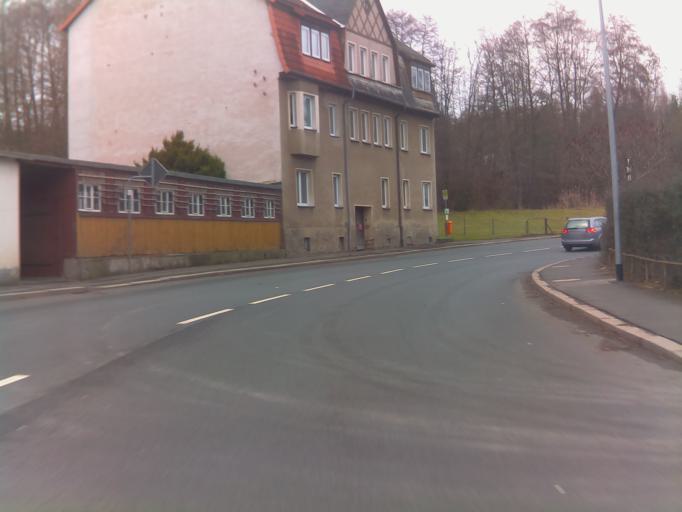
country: DE
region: Thuringia
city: Auma
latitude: 50.7034
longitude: 11.8958
